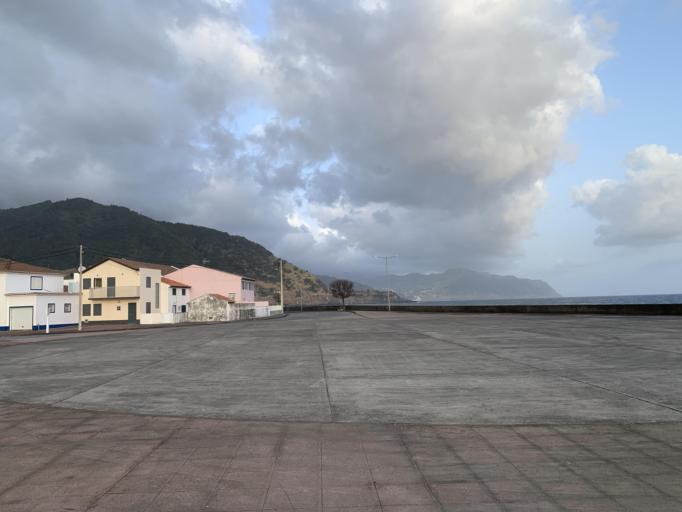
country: PT
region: Azores
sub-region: Povoacao
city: Furnas
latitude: 37.7289
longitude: -25.3077
